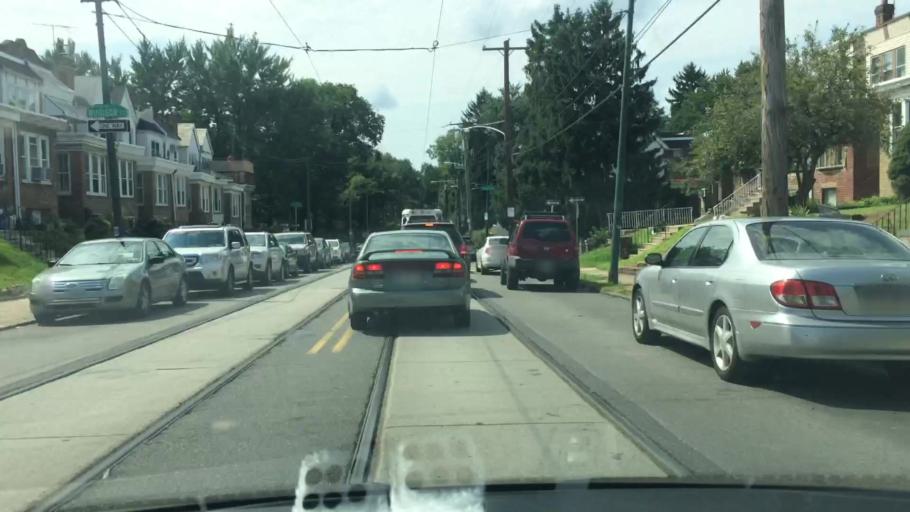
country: US
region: Pennsylvania
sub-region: Delaware County
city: Yeadon
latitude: 39.9292
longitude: -75.2417
